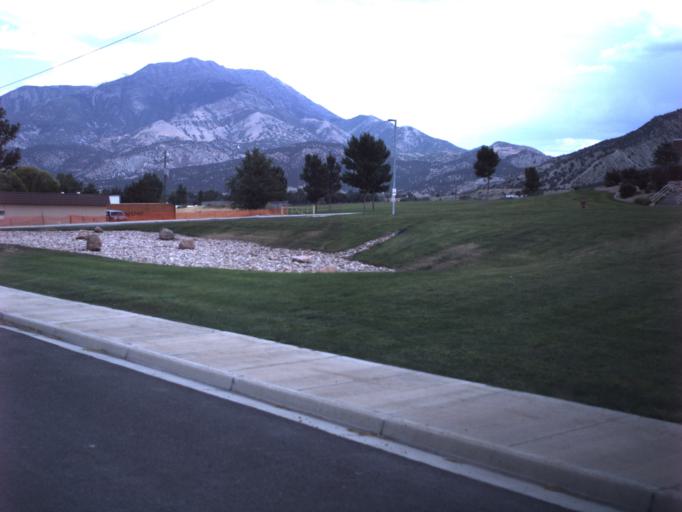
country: US
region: Utah
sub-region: Juab County
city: Nephi
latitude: 39.6915
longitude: -111.8360
